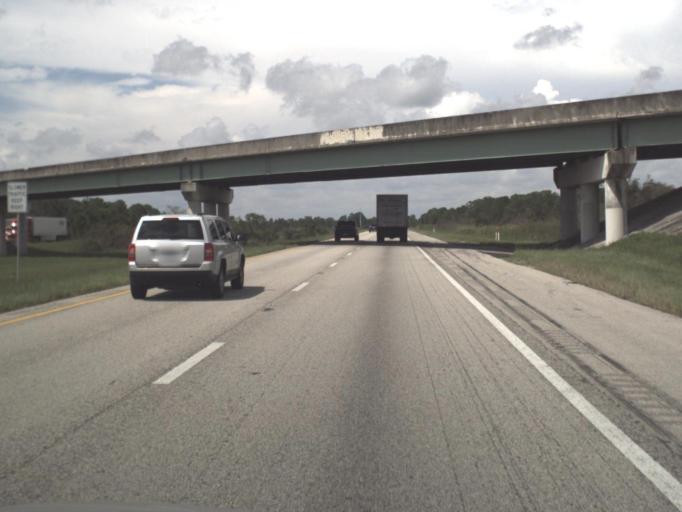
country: US
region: Florida
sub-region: Lee County
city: Suncoast Estates
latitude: 26.8102
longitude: -81.9308
